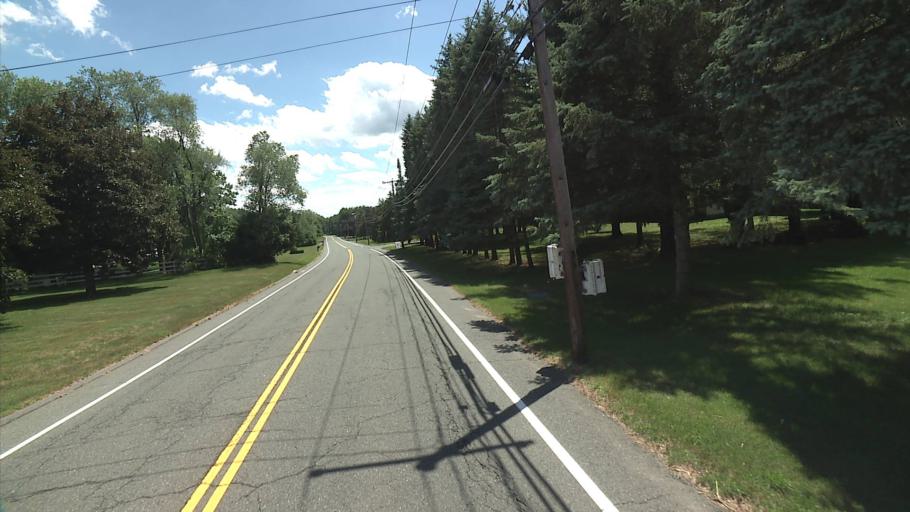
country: US
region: Connecticut
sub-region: Tolland County
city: Somers
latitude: 42.0013
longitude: -72.4887
